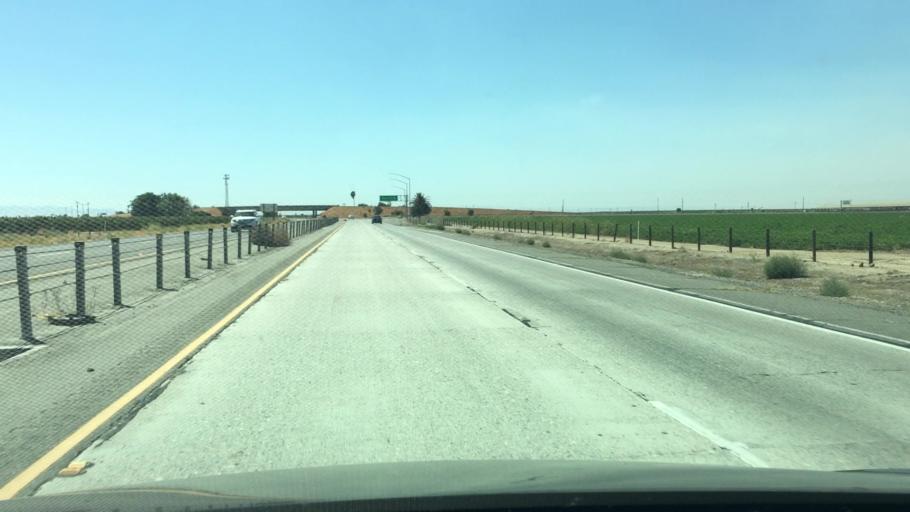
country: US
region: California
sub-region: Merced County
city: Dos Palos
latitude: 37.0837
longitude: -120.4862
